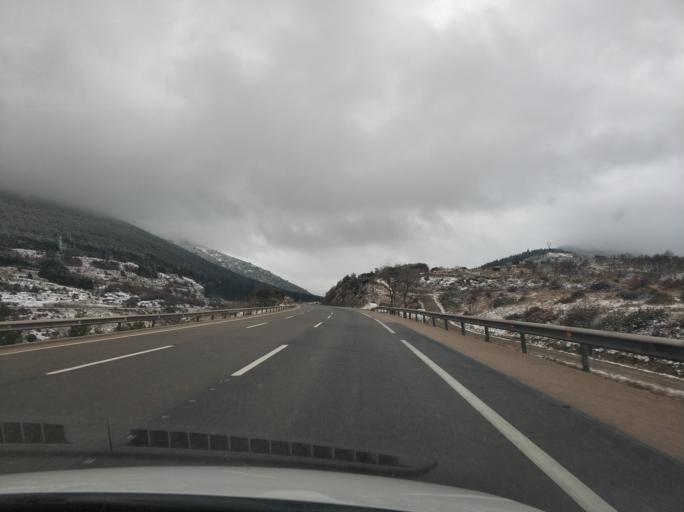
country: ES
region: Madrid
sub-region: Provincia de Madrid
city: Somosierra
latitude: 41.1749
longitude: -3.5829
